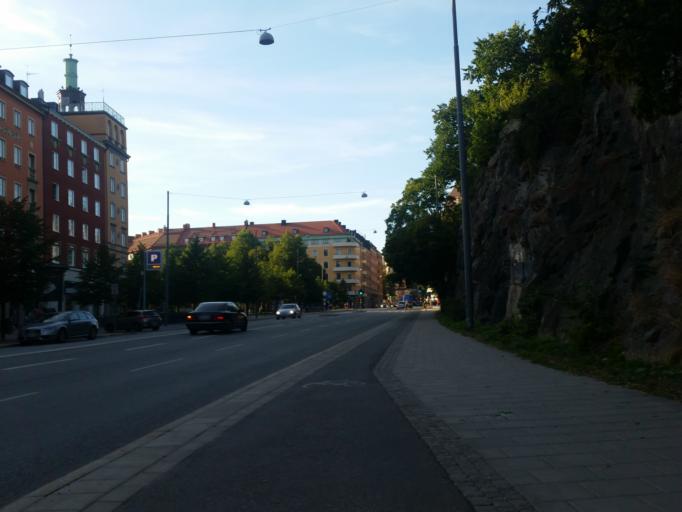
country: SE
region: Stockholm
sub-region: Stockholms Kommun
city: Stockholm
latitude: 59.3384
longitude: 18.0405
